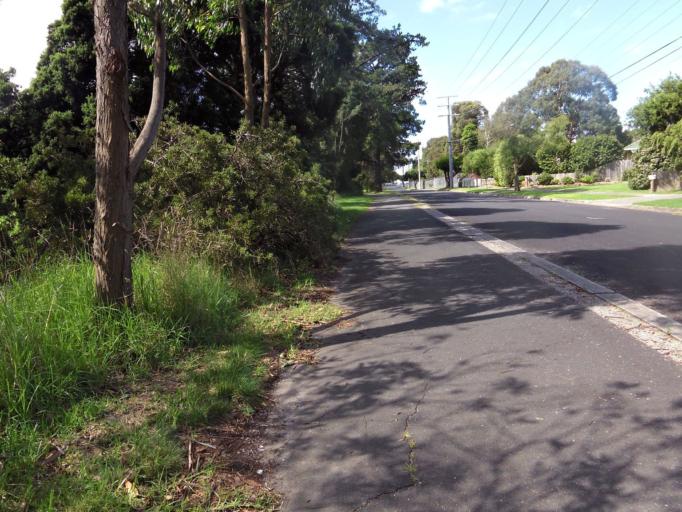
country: AU
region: Victoria
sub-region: Maroondah
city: Ringwood East
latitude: -37.8138
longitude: 145.2443
